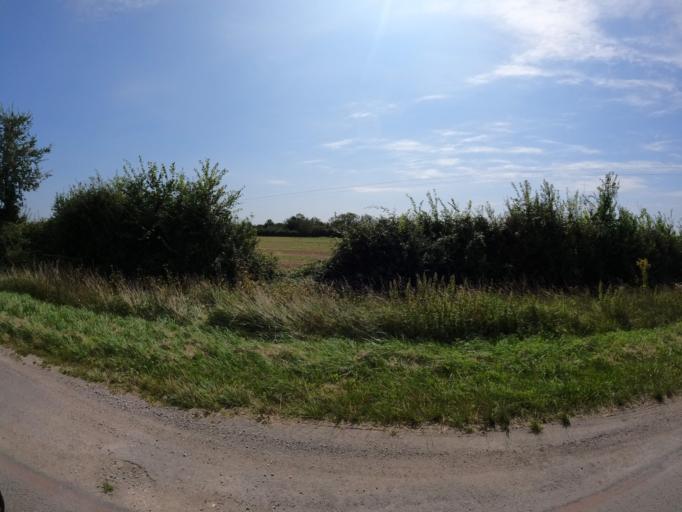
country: FR
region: Poitou-Charentes
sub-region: Departement des Deux-Sevres
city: Bessines
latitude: 46.2899
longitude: -0.5087
